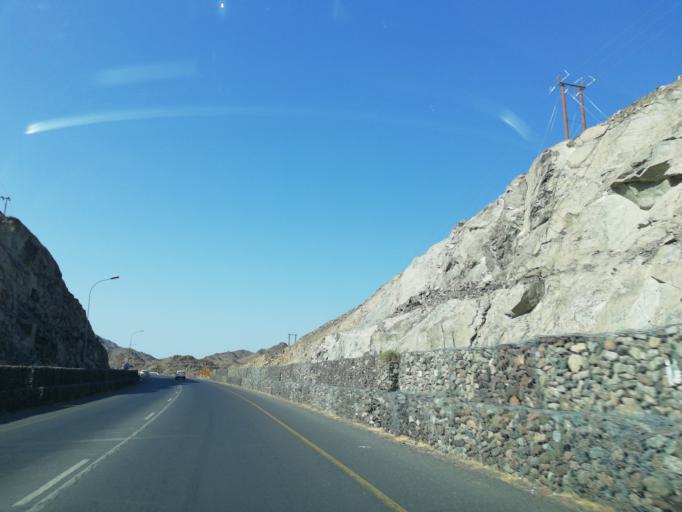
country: OM
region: Ash Sharqiyah
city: Ibra'
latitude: 22.8203
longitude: 58.1671
